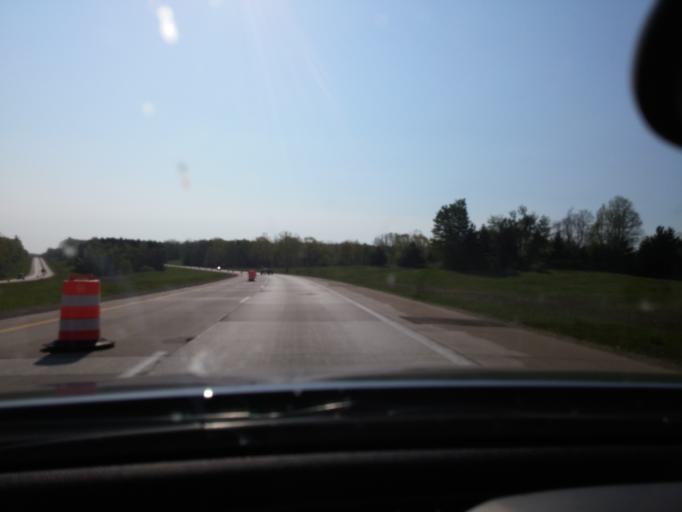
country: US
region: Michigan
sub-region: Lapeer County
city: Lapeer
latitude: 43.0073
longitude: -83.2175
